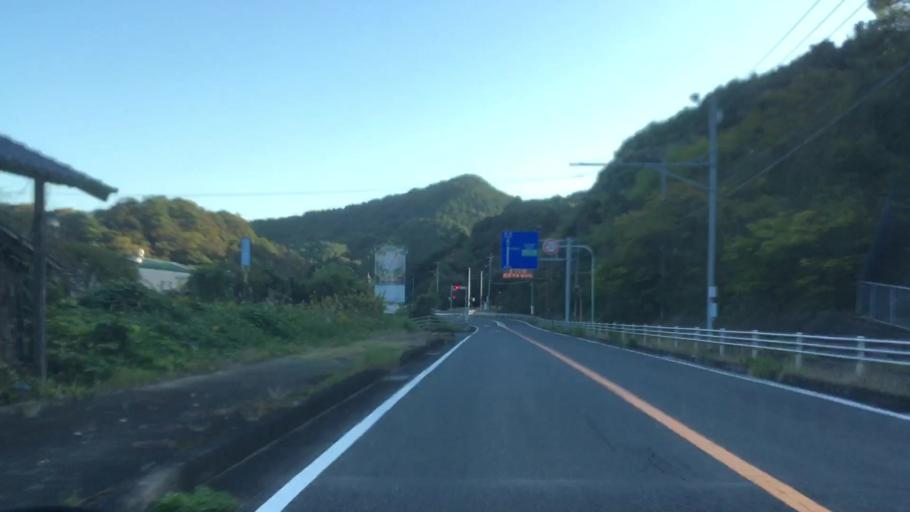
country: JP
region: Nagasaki
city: Sasebo
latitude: 32.9983
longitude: 129.7321
